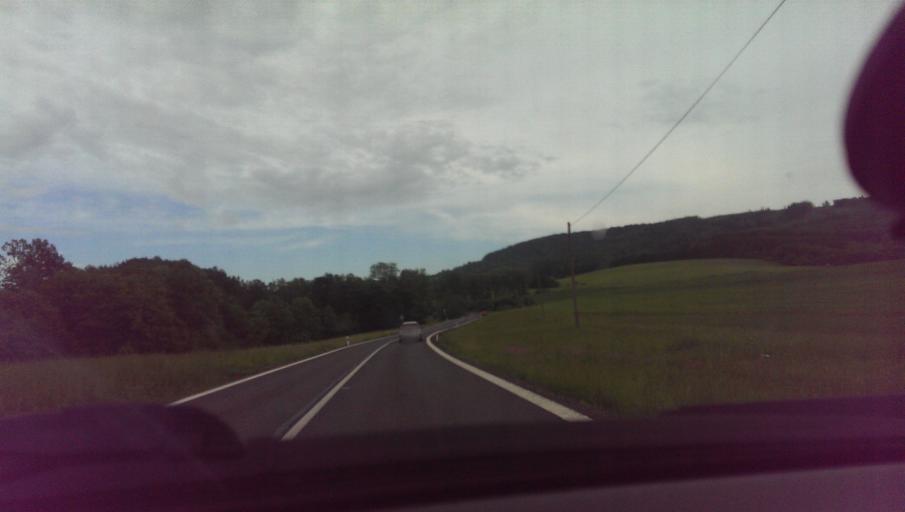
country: CZ
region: Zlin
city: Ujezd
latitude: 49.2271
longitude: 17.9282
